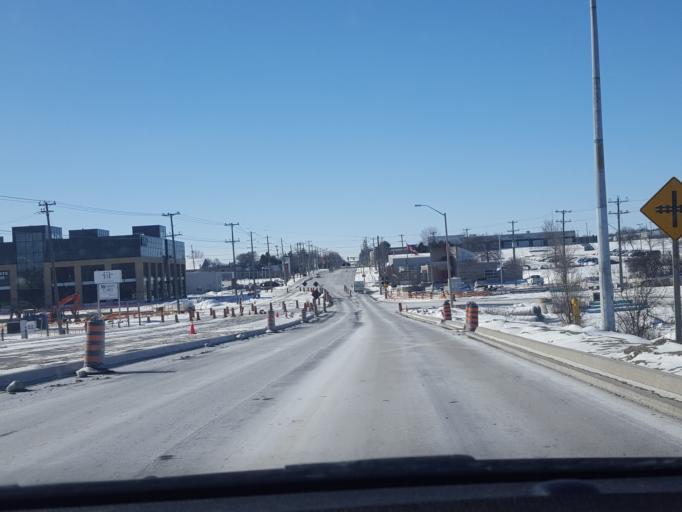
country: CA
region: Ontario
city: Waterloo
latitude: 43.4986
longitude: -80.5421
